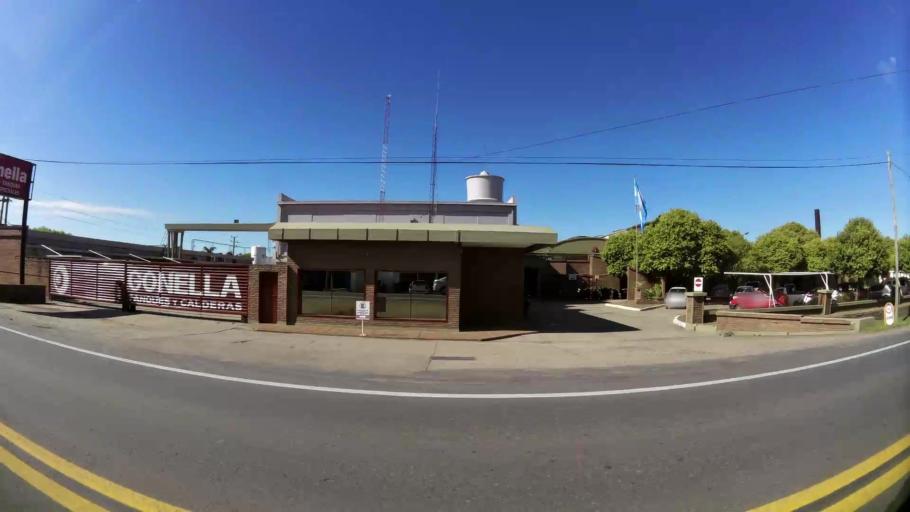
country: AR
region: Santa Fe
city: Esperanza
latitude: -31.4472
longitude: -60.9106
